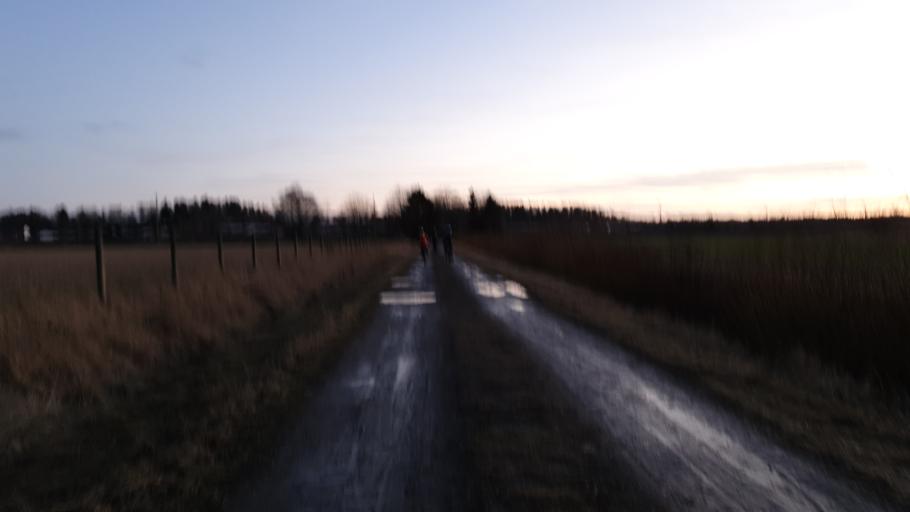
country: FI
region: Uusimaa
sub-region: Helsinki
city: Vantaa
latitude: 60.2695
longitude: 24.9483
